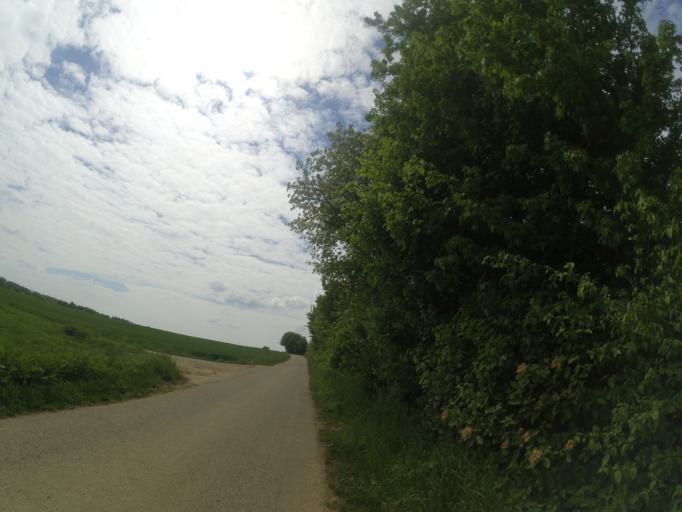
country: DE
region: Baden-Wuerttemberg
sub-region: Tuebingen Region
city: Berghulen
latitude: 48.4448
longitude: 9.7729
